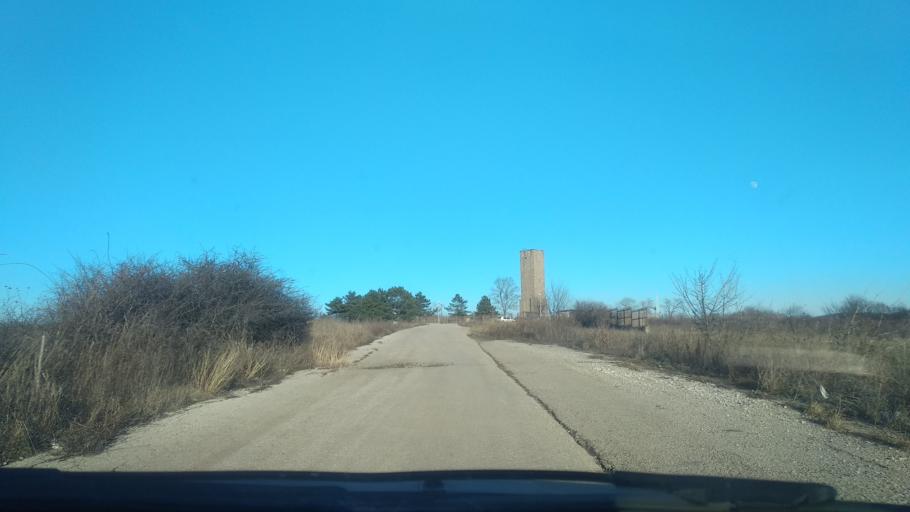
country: XK
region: Pristina
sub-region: Kosovo Polje
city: Kosovo Polje
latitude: 42.6895
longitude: 21.1209
